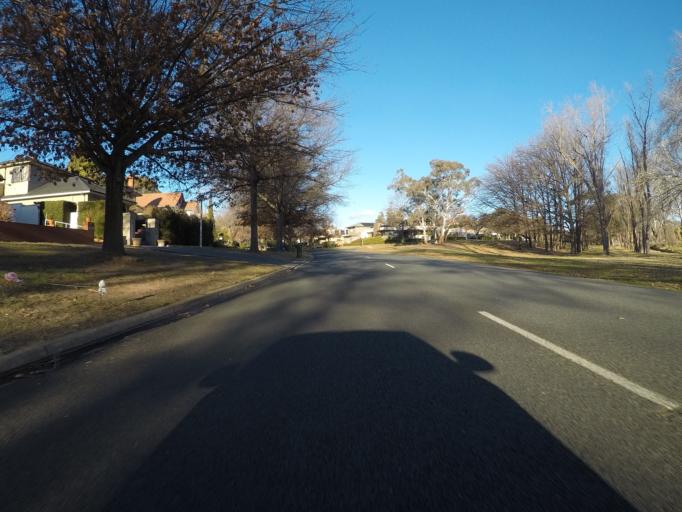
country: AU
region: Australian Capital Territory
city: Forrest
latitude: -35.3041
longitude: 149.1023
